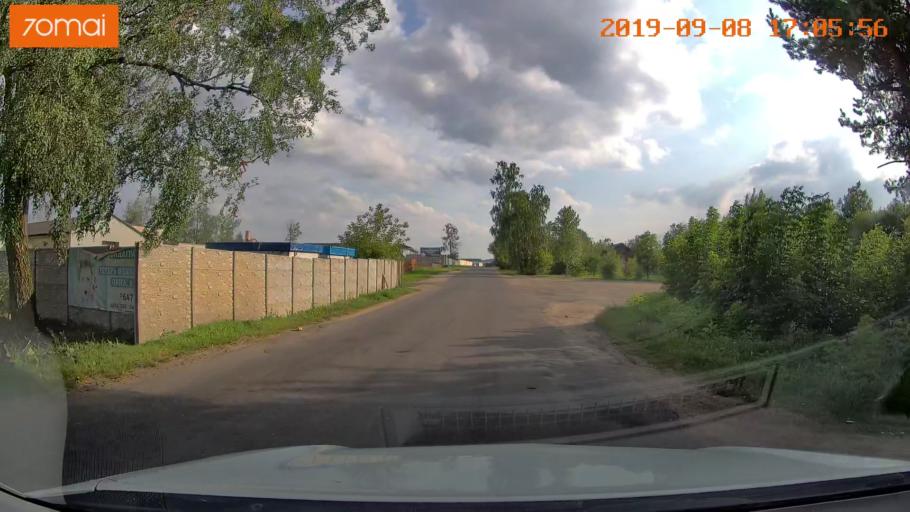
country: BY
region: Grodnenskaya
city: Hrodna
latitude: 53.6748
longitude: 23.9534
